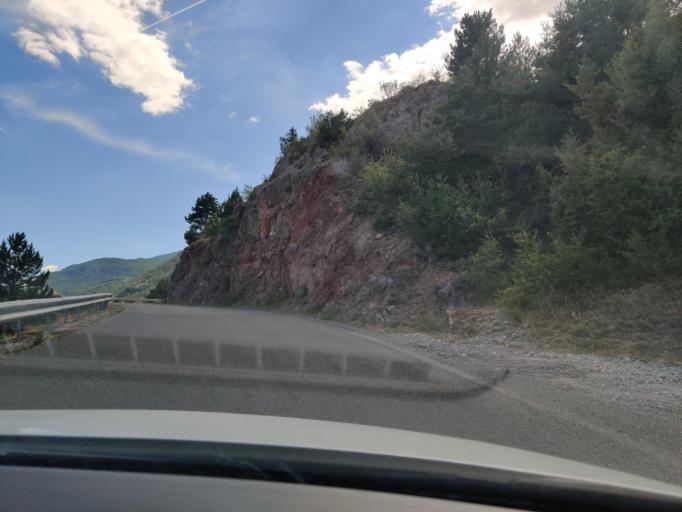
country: FR
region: Provence-Alpes-Cote d'Azur
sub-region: Departement des Hautes-Alpes
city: Saint-Martin-de-Queyrieres
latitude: 44.7412
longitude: 6.5728
